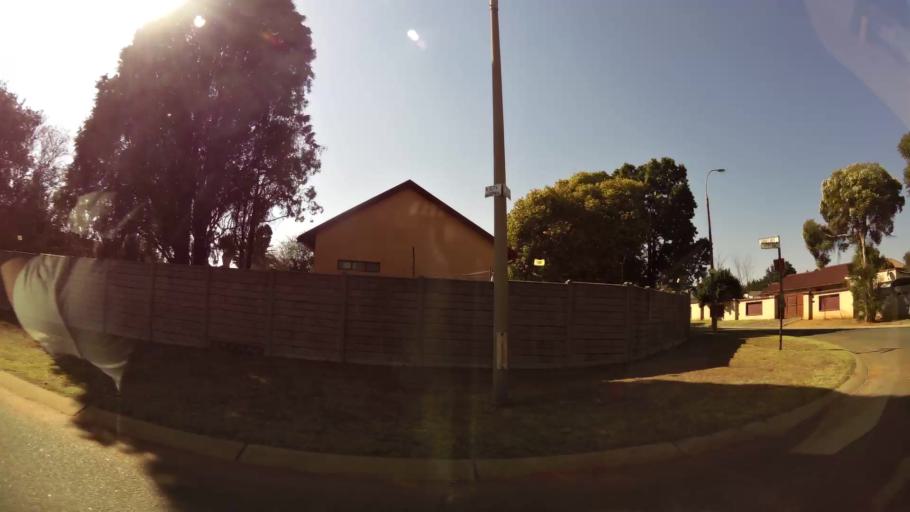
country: ZA
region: Gauteng
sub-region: City of Johannesburg Metropolitan Municipality
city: Modderfontein
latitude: -26.0514
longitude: 28.2016
